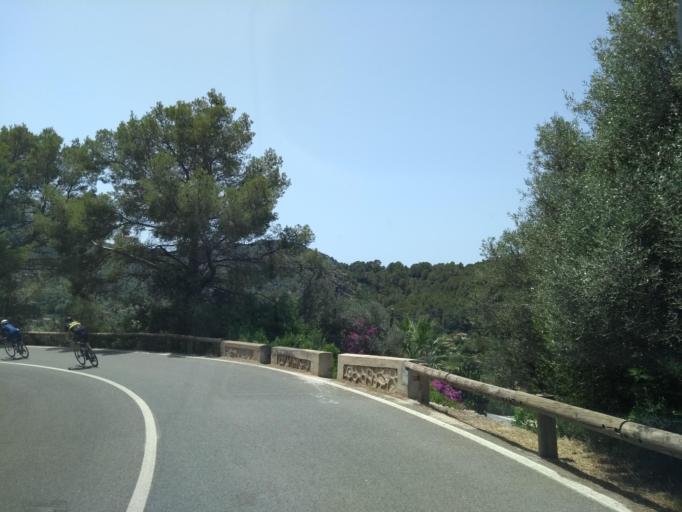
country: ES
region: Balearic Islands
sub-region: Illes Balears
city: Soller
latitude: 39.7841
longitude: 2.7111
